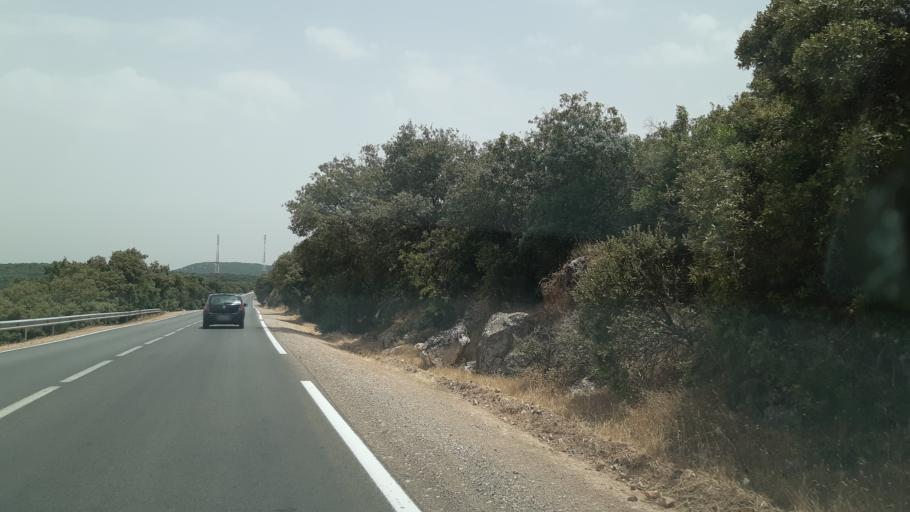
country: MA
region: Meknes-Tafilalet
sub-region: Ifrane
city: Ifrane
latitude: 33.6580
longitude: -5.0549
